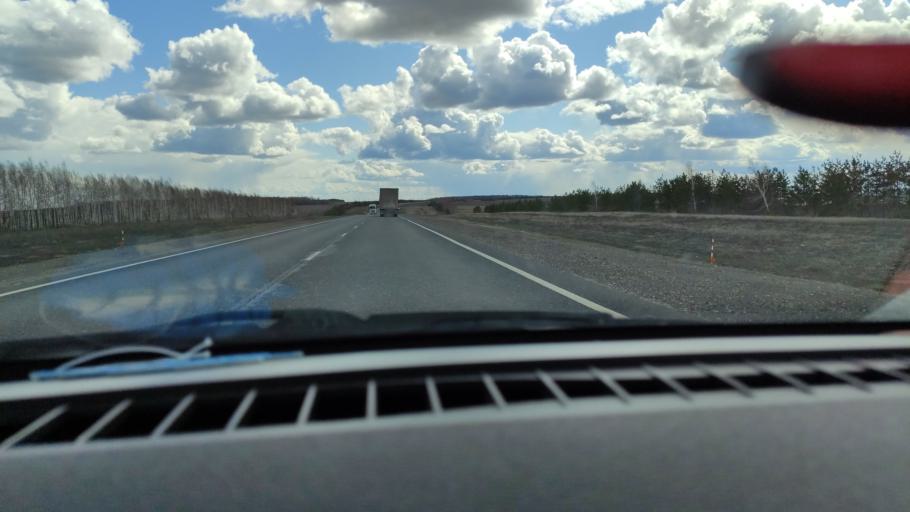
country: RU
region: Samara
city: Syzran'
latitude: 52.8867
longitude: 48.2938
